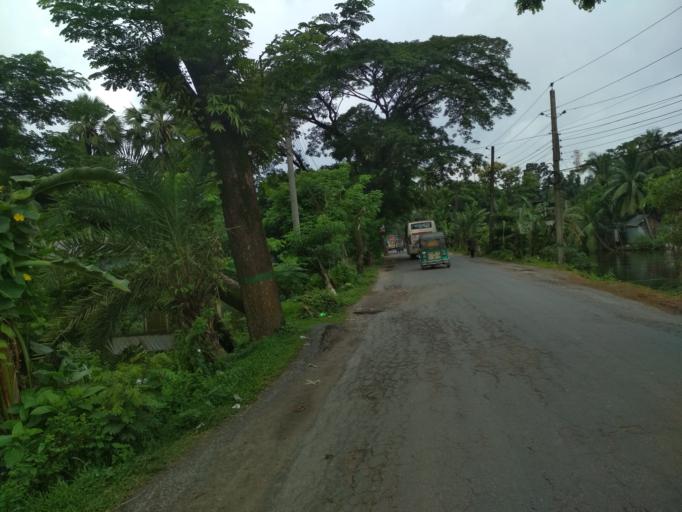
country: BD
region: Chittagong
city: Lakshmipur
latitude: 22.9461
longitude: 90.8161
